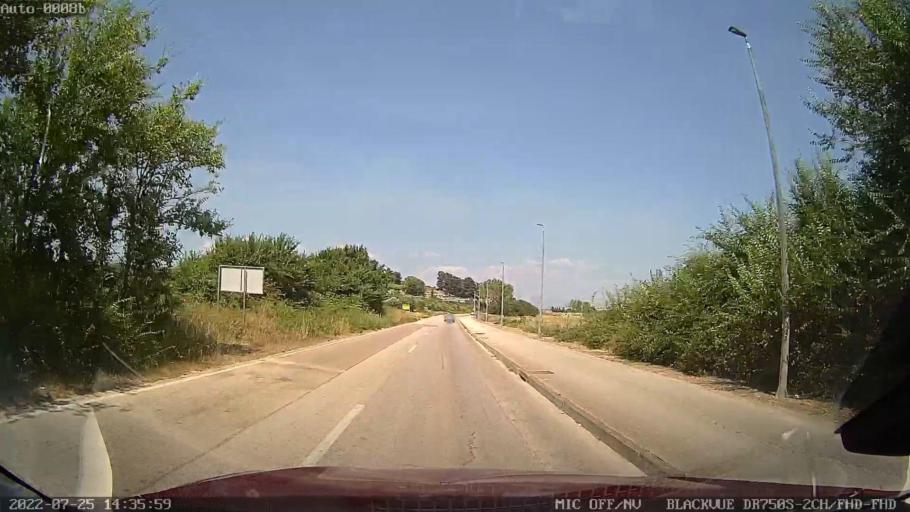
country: HR
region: Zadarska
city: Galovac
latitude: 44.1079
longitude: 15.3816
